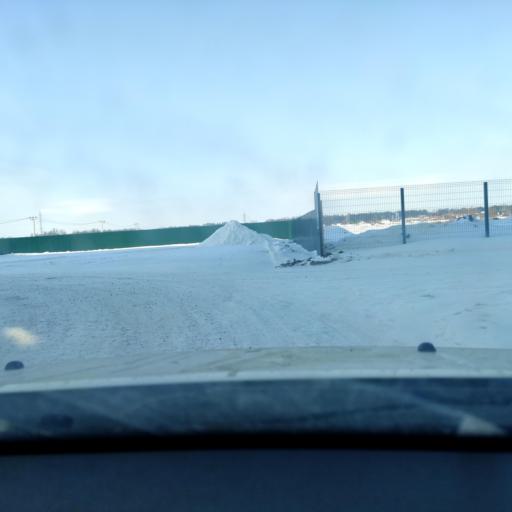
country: RU
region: Bashkortostan
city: Ufa
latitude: 54.7808
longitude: 55.9613
